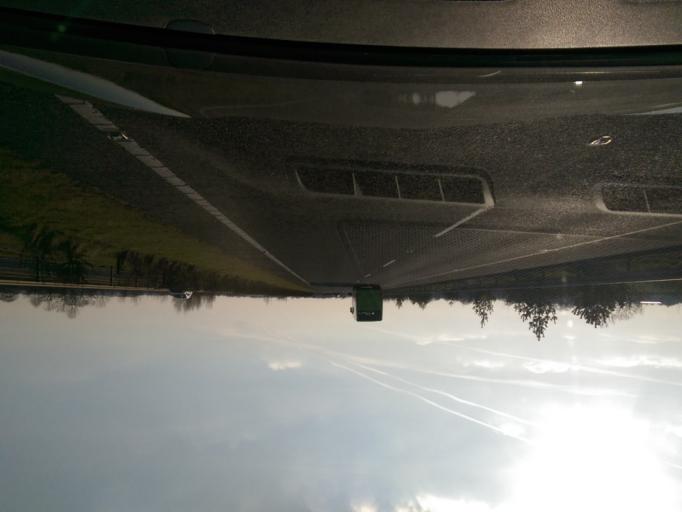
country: IE
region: Leinster
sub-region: Kildare
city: Monasterevin
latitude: 53.1143
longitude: -7.0826
